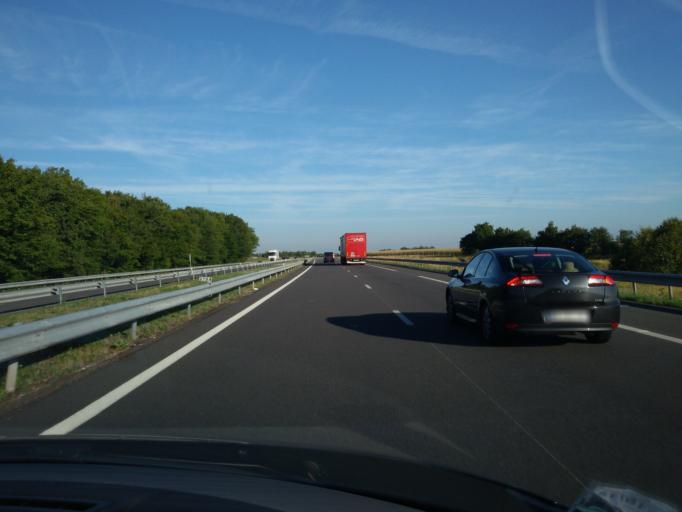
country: FR
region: Centre
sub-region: Departement du Cher
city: Plaimpied-Givaudins
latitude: 46.9814
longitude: 2.4186
